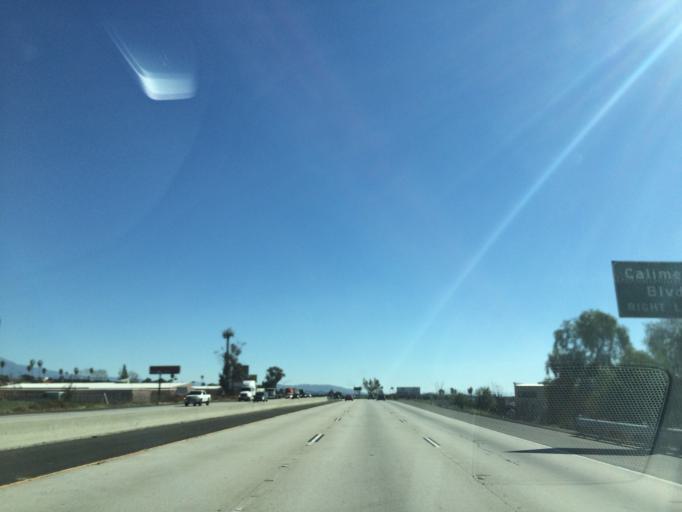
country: US
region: California
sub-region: Riverside County
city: Calimesa
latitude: 33.9995
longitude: -117.0627
